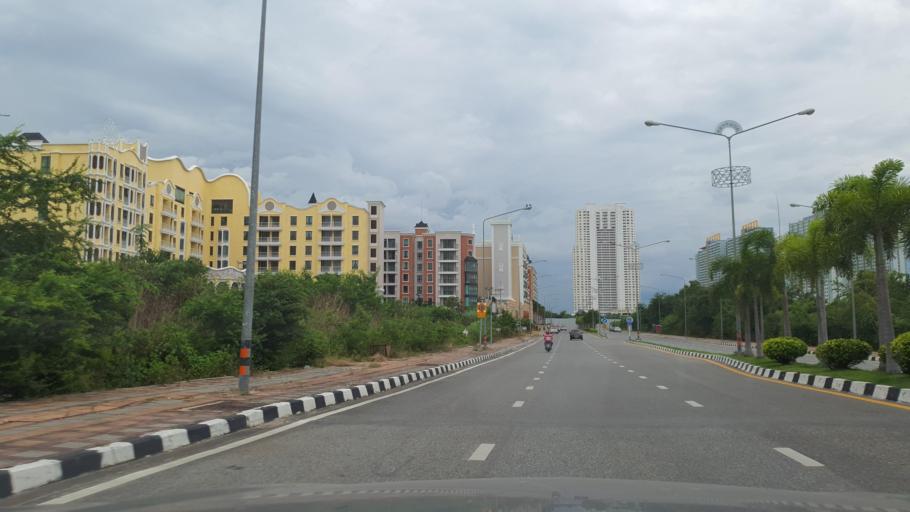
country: TH
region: Chon Buri
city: Phatthaya
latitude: 12.8711
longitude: 100.8997
